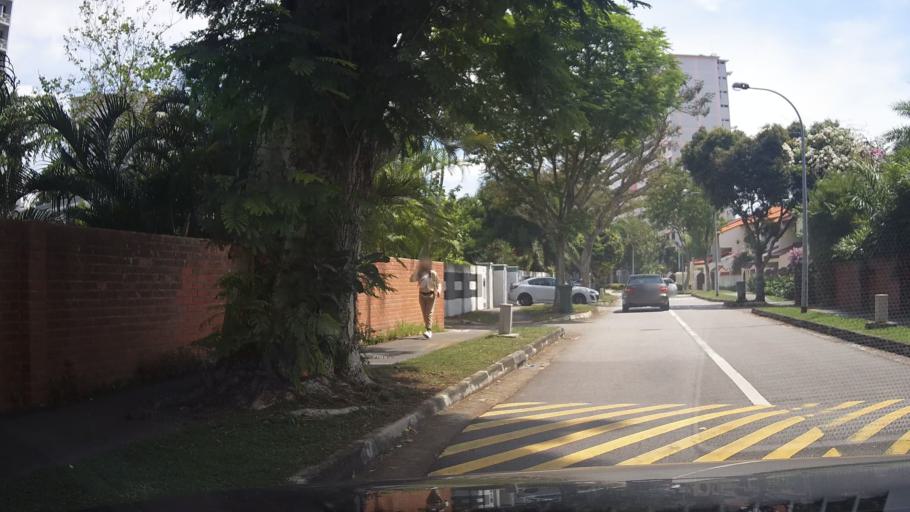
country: SG
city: Singapore
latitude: 1.3109
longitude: 103.8960
